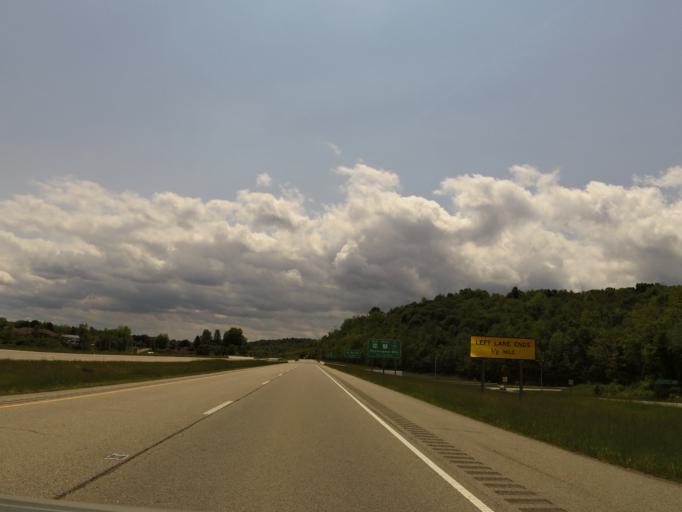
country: US
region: Ohio
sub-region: Meigs County
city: Pomeroy
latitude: 39.0597
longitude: -82.0178
